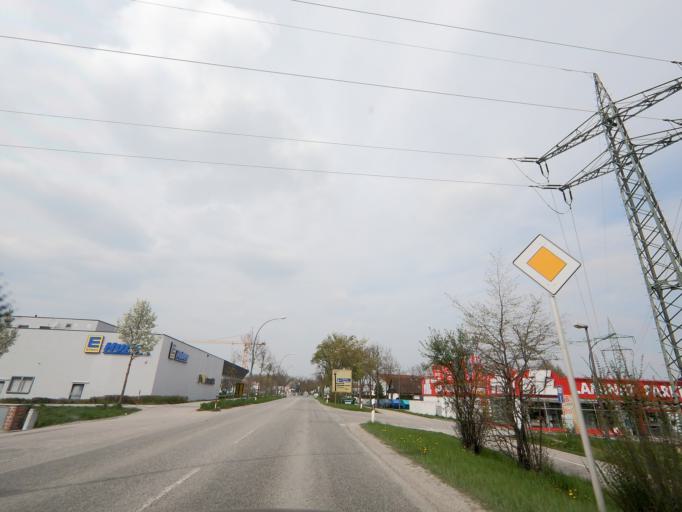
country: DE
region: Bavaria
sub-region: Lower Bavaria
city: Landshut
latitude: 48.5585
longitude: 12.1362
